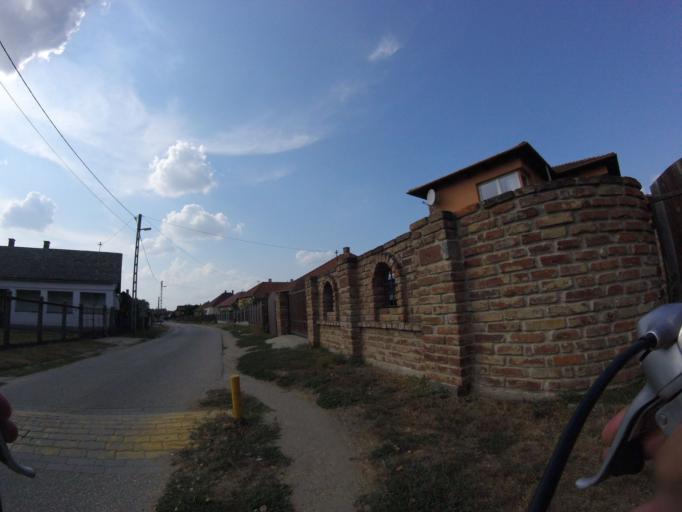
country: HU
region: Szabolcs-Szatmar-Bereg
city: Nyirpazony
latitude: 48.0140
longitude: 21.8307
